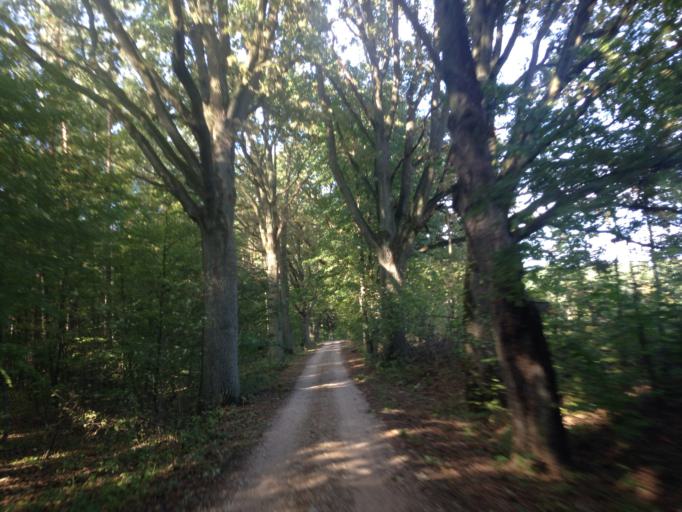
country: PL
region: Warmian-Masurian Voivodeship
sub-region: Powiat dzialdowski
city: Lidzbark
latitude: 53.2489
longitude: 19.7637
